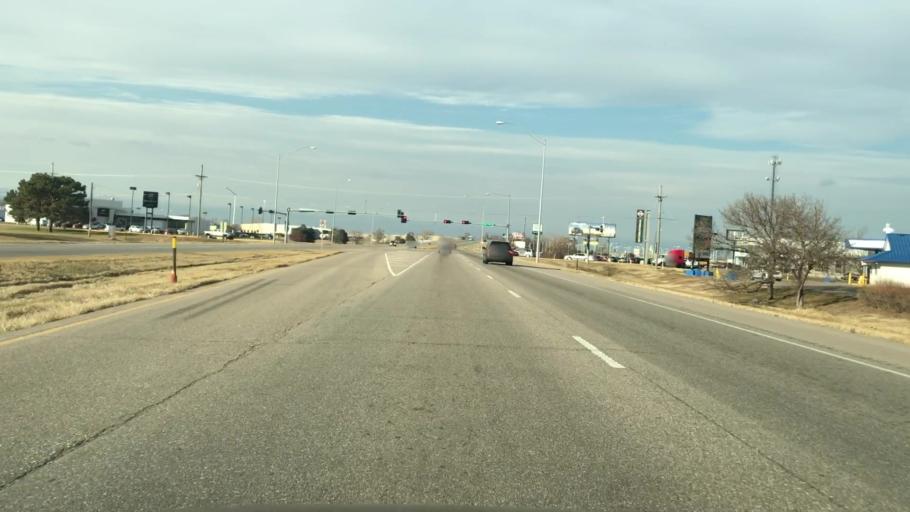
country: US
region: Nebraska
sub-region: Hall County
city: Grand Island
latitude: 40.9012
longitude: -98.3807
